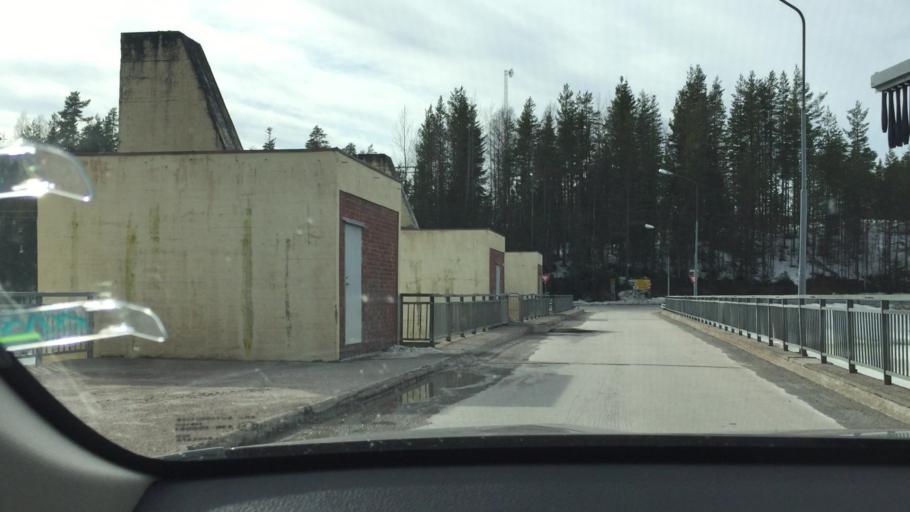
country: NO
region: Hedmark
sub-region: Trysil
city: Innbygda
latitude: 61.0658
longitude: 12.5817
